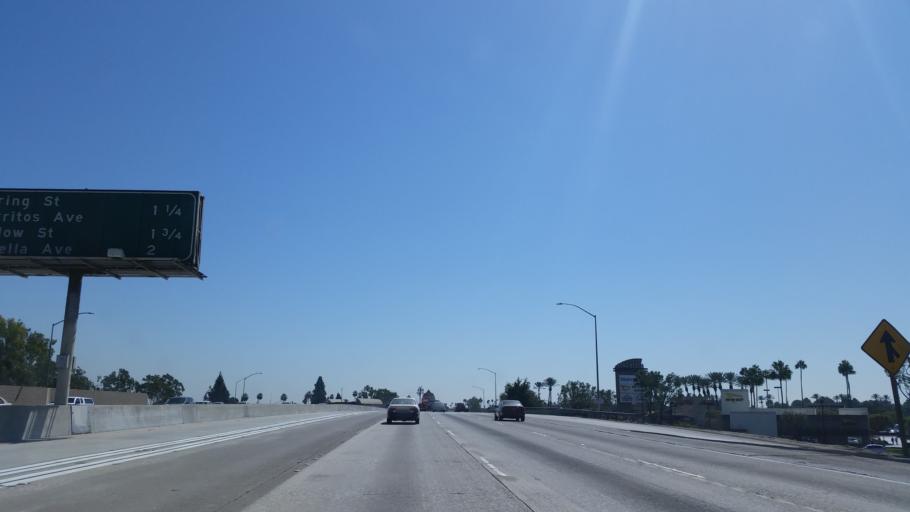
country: US
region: California
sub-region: Los Angeles County
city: Hawaiian Gardens
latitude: 33.8329
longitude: -118.0850
